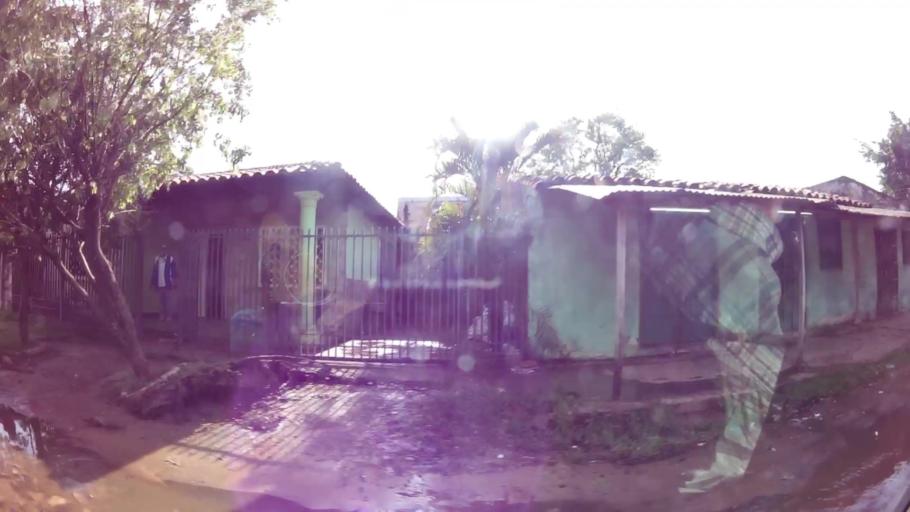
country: PY
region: Central
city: Limpio
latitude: -25.1703
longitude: -57.4890
